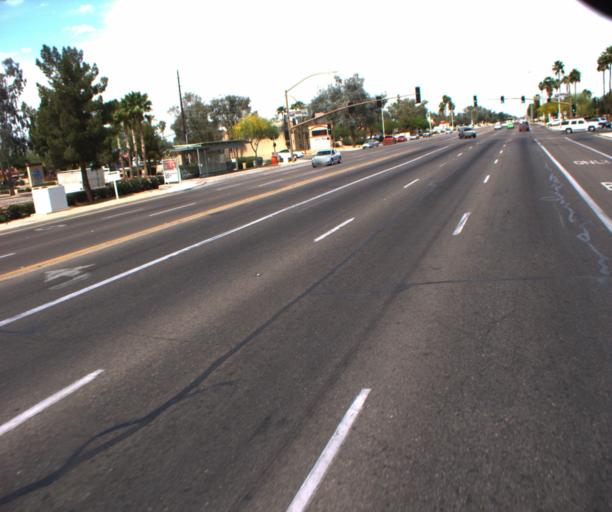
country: US
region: Arizona
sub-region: Maricopa County
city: San Carlos
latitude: 33.3343
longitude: -111.8416
